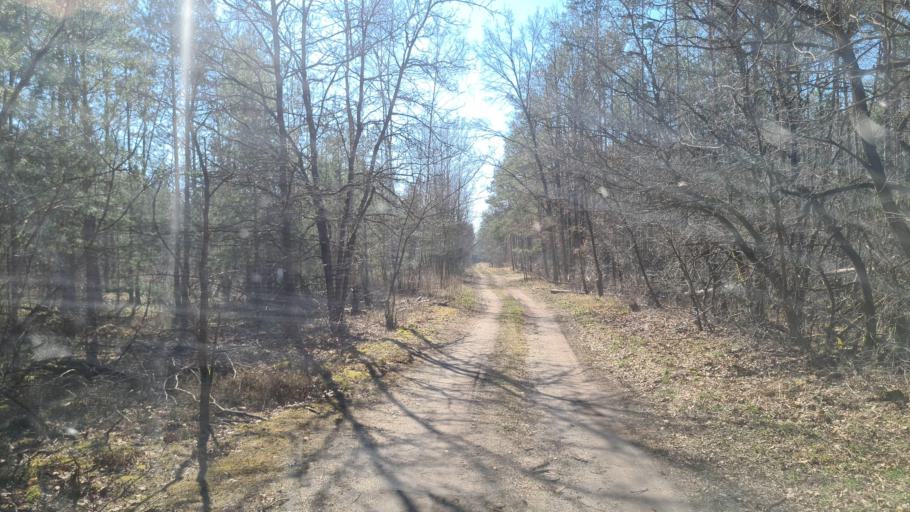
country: DE
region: Brandenburg
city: Finsterwalde
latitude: 51.5952
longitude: 13.7281
